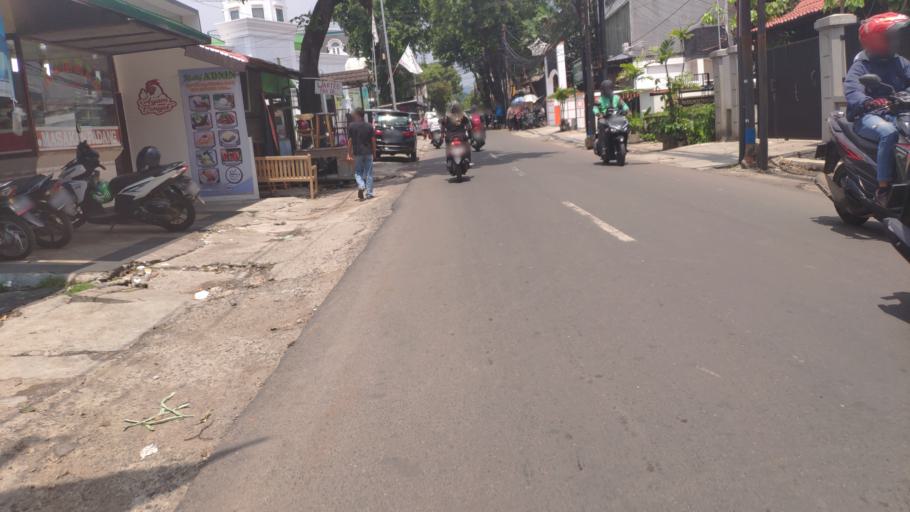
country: ID
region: Jakarta Raya
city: Jakarta
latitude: -6.2678
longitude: 106.8239
